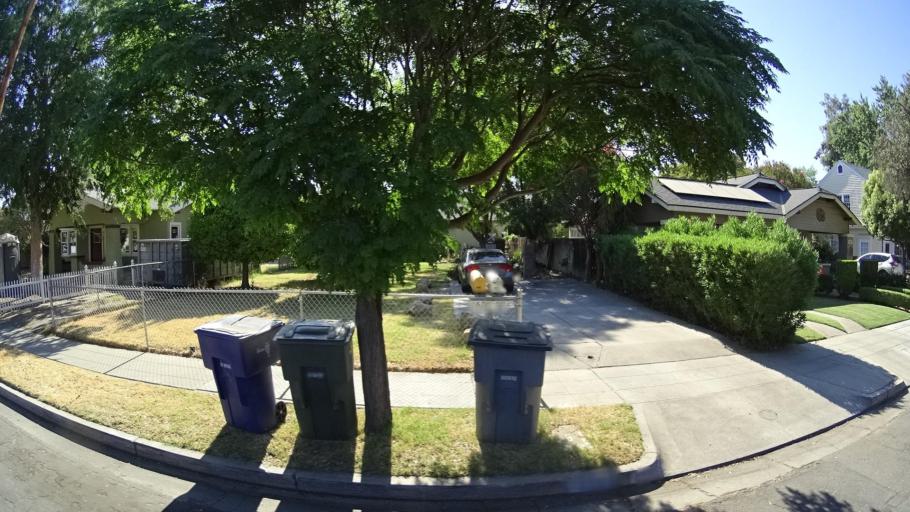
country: US
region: California
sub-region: Fresno County
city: Fresno
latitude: 36.7635
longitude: -119.8097
